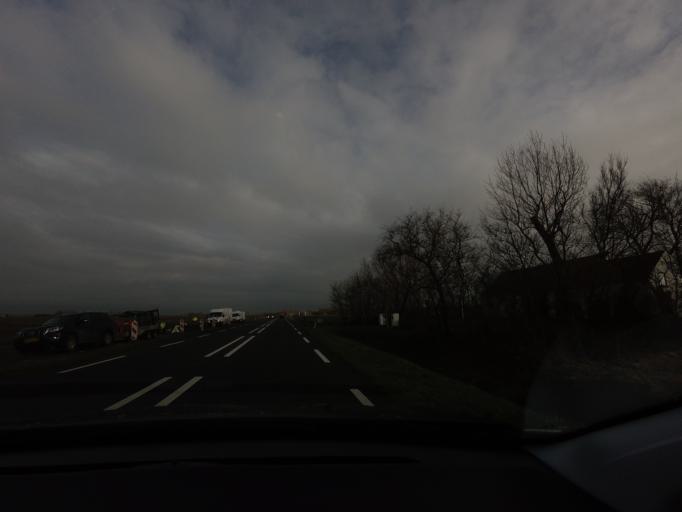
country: NL
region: Zeeland
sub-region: Schouwen-Duiveland
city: Renesse
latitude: 51.7004
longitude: 3.7807
